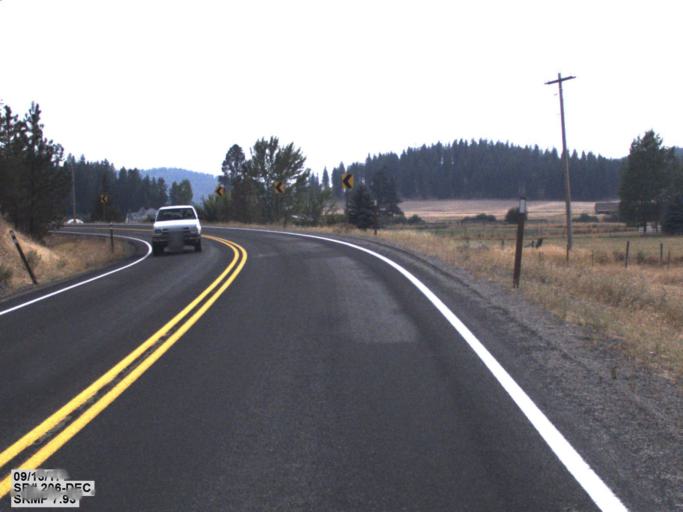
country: US
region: Washington
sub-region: Spokane County
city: Trentwood
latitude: 47.8168
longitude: -117.2148
